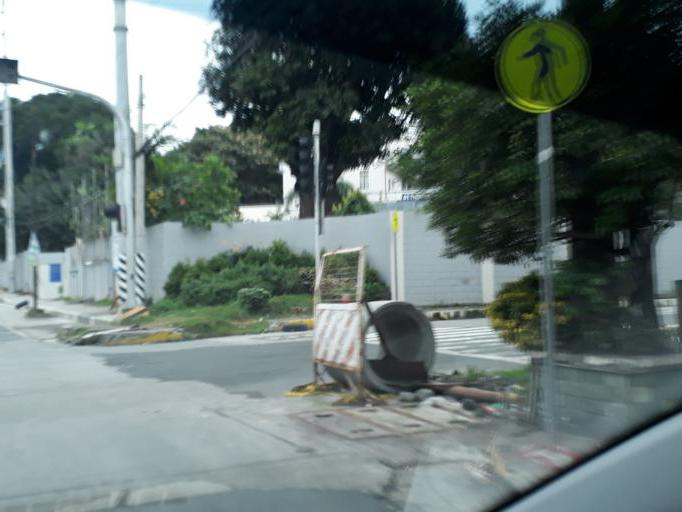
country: PH
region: Calabarzon
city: Del Monte
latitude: 14.6261
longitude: 121.0015
